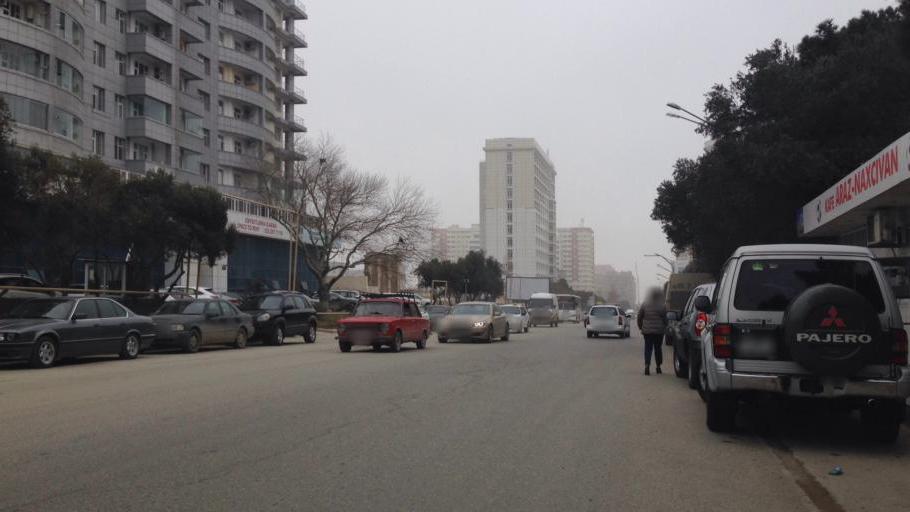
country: AZ
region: Baki
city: Baku
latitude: 40.3883
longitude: 49.8759
